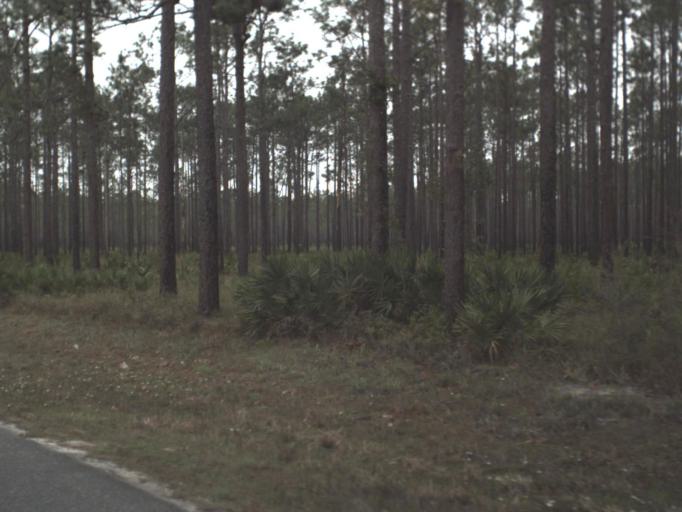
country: US
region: Florida
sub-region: Gulf County
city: Wewahitchka
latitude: 29.9867
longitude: -84.9761
